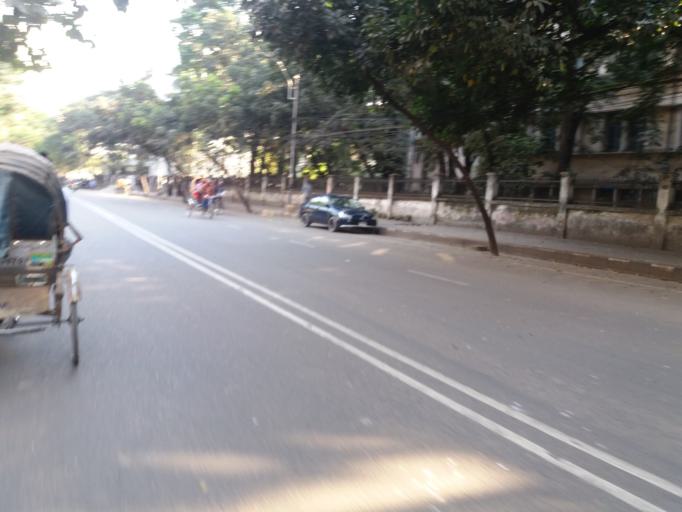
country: BD
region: Dhaka
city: Azimpur
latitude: 23.7252
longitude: 90.3933
